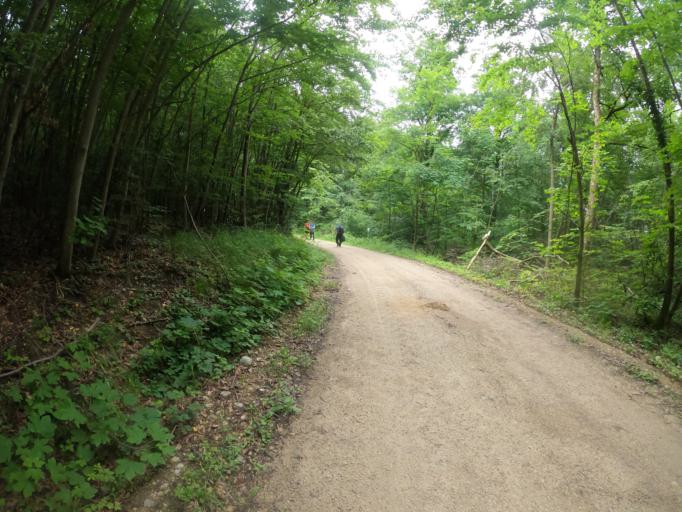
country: DE
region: Bavaria
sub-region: Upper Franconia
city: Litzendorf
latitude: 49.9248
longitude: 11.0344
